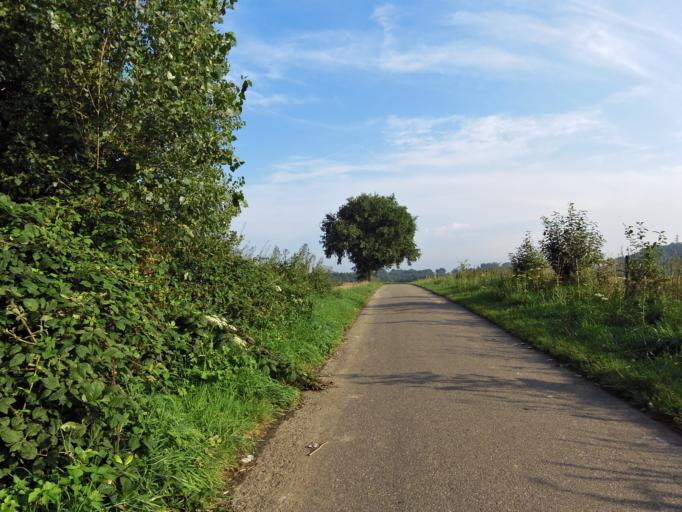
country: NL
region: Limburg
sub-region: Gemeente Kerkrade
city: Kerkrade
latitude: 50.9046
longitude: 6.0636
